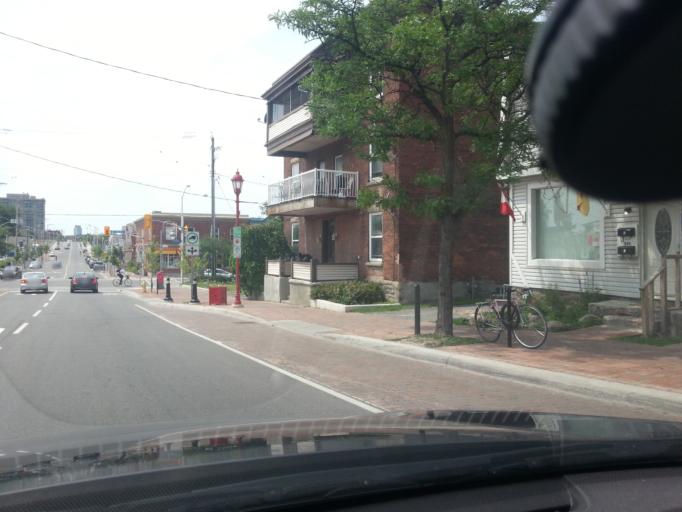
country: CA
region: Ontario
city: Ottawa
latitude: 45.4087
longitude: -75.7134
